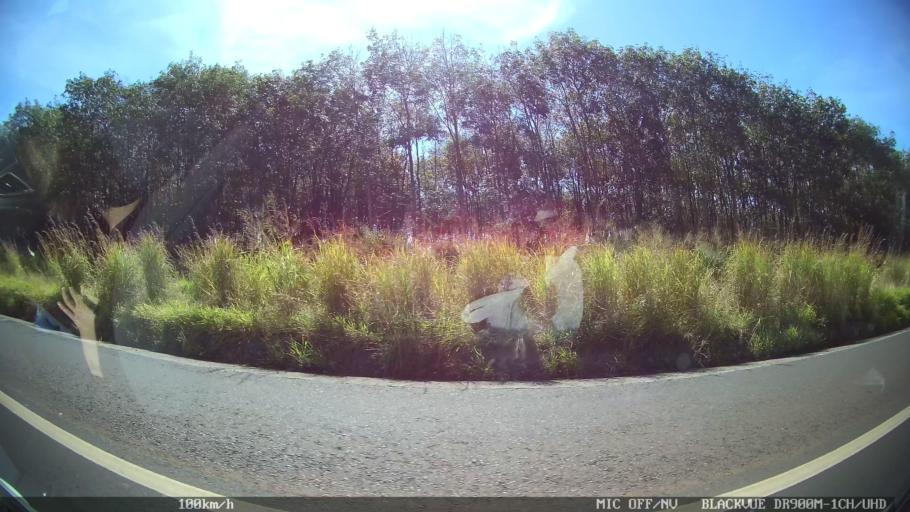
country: BR
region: Sao Paulo
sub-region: Franca
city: Franca
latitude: -20.5585
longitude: -47.5464
